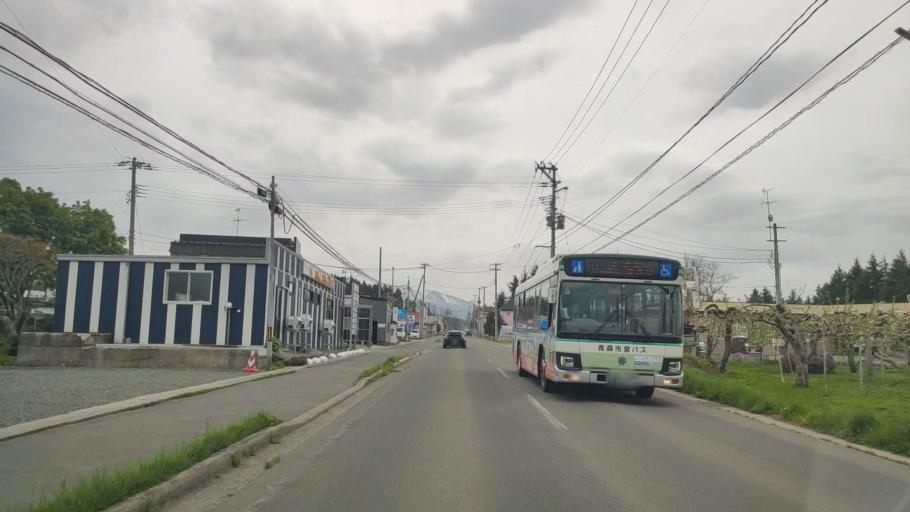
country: JP
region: Aomori
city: Aomori Shi
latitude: 40.7836
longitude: 140.7908
